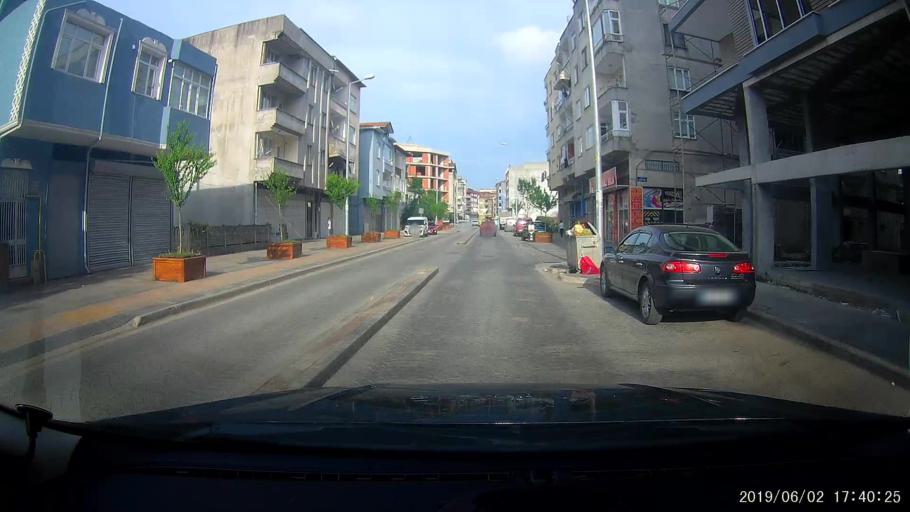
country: TR
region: Samsun
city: Terme
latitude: 41.2112
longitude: 36.9656
